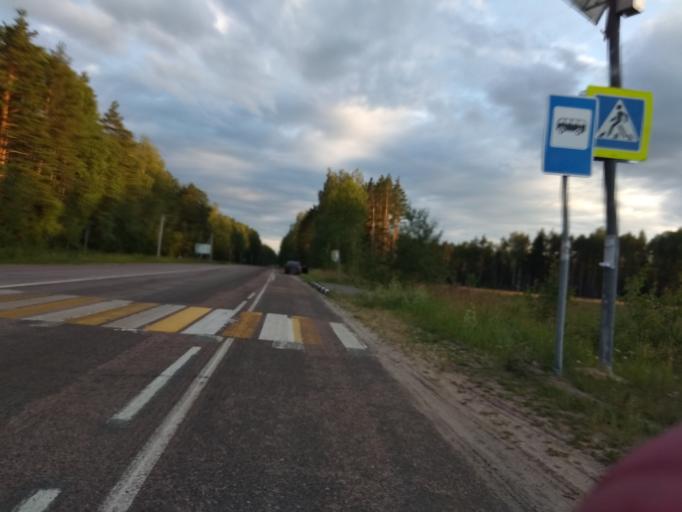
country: RU
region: Moskovskaya
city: Misheronskiy
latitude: 55.6184
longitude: 39.7261
